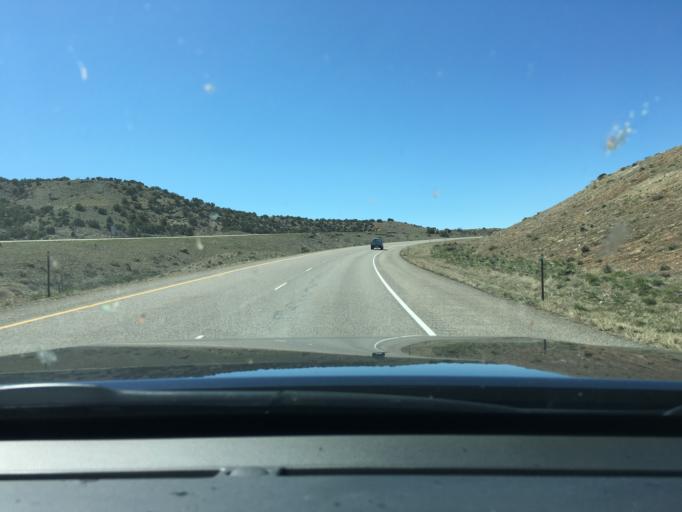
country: US
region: Colorado
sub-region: Mesa County
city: Loma
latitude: 39.1886
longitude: -109.0314
